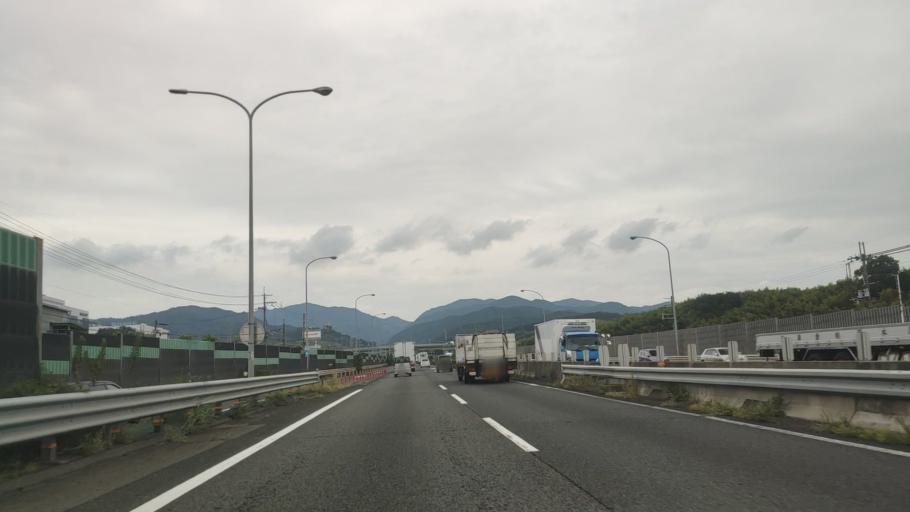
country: JP
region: Nara
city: Tenri
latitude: 34.6176
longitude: 135.8372
